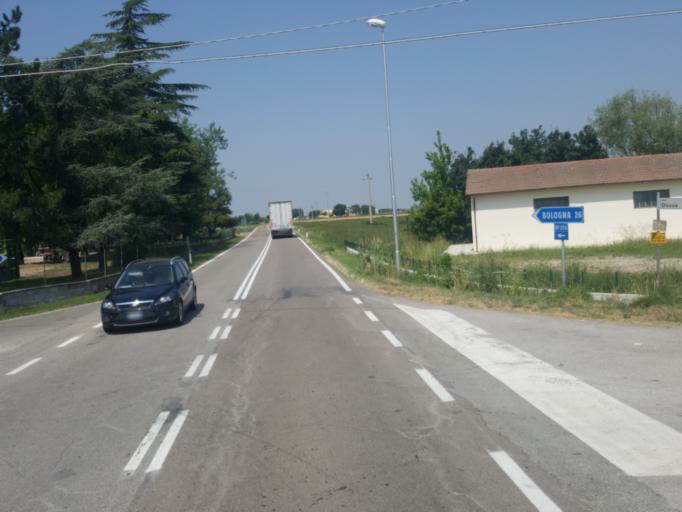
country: IT
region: Emilia-Romagna
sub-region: Provincia di Bologna
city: Sesto Imolese
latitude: 44.4666
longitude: 11.7214
